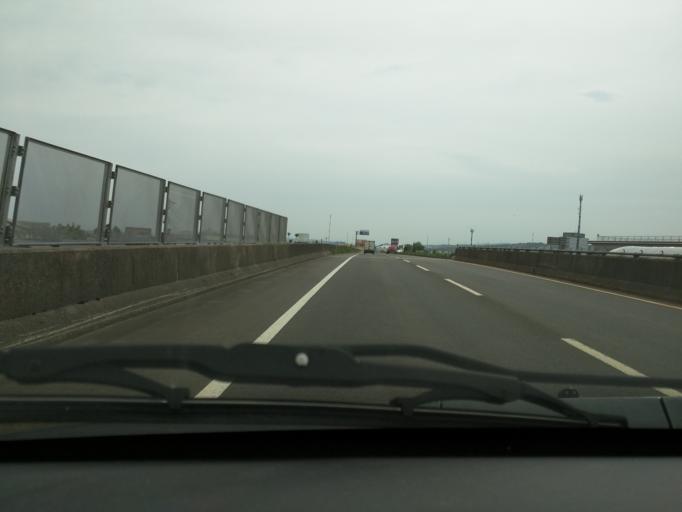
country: JP
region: Niigata
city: Nagaoka
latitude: 37.4517
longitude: 138.8017
